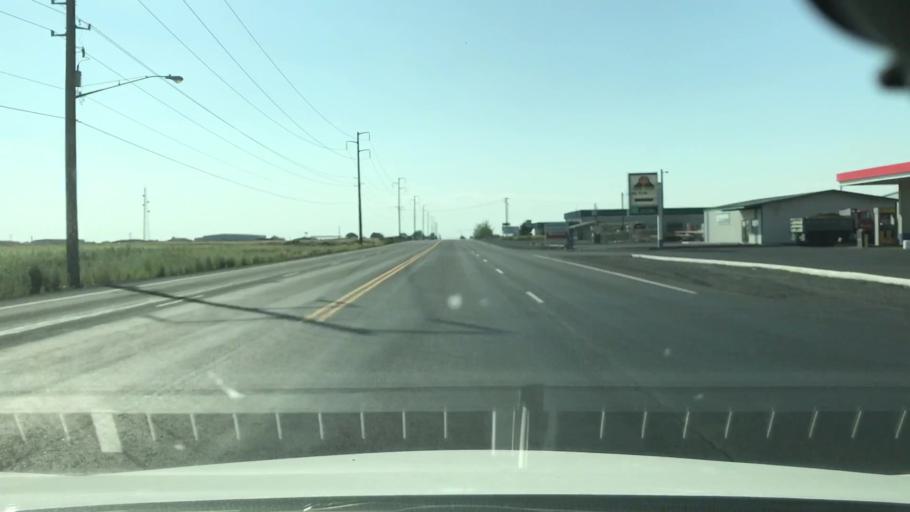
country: US
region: Washington
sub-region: Grant County
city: Moses Lake
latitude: 47.1310
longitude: -119.2384
